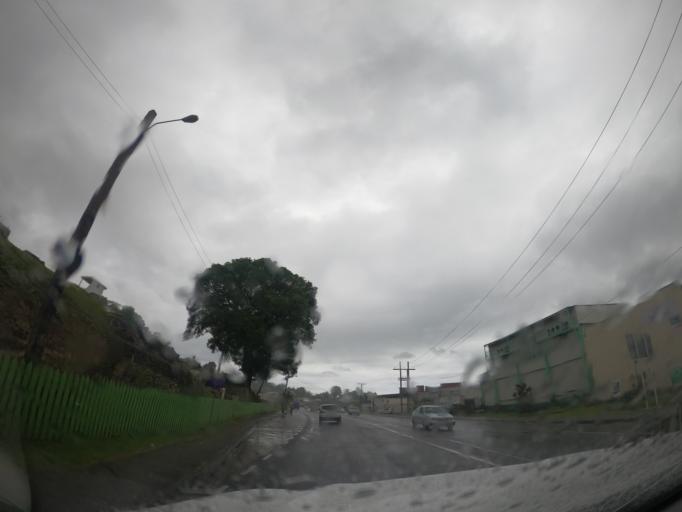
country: FJ
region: Central
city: Suva
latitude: -18.1172
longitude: 178.4310
